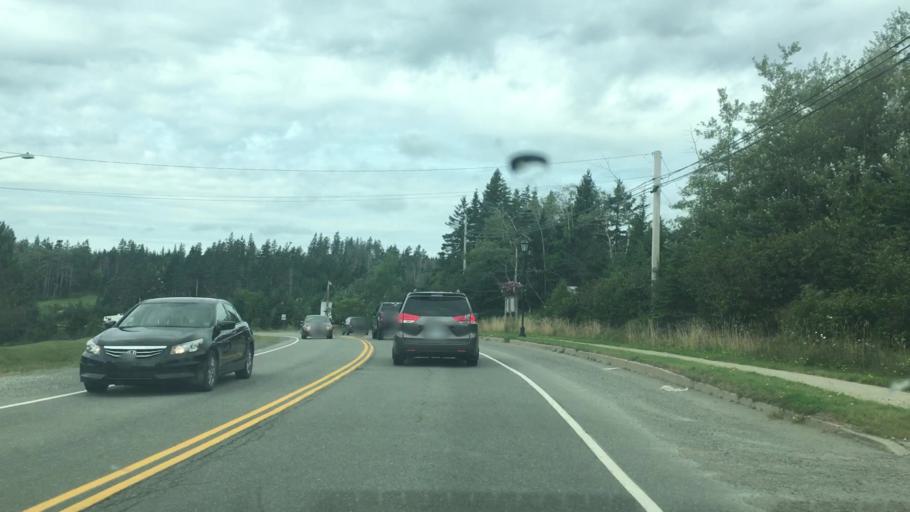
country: CA
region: Nova Scotia
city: Princeville
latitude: 45.6554
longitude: -60.8947
